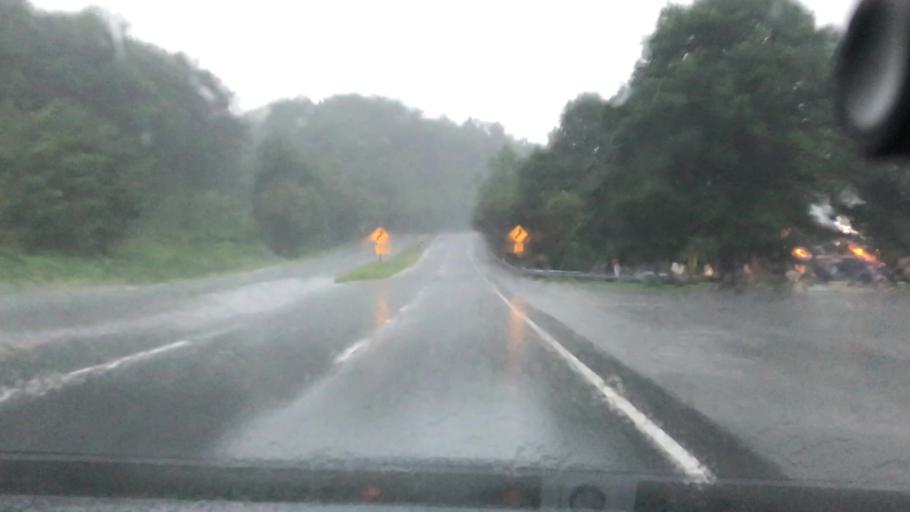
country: US
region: Virginia
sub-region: Giles County
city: Pearisburg
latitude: 37.3483
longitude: -80.7617
